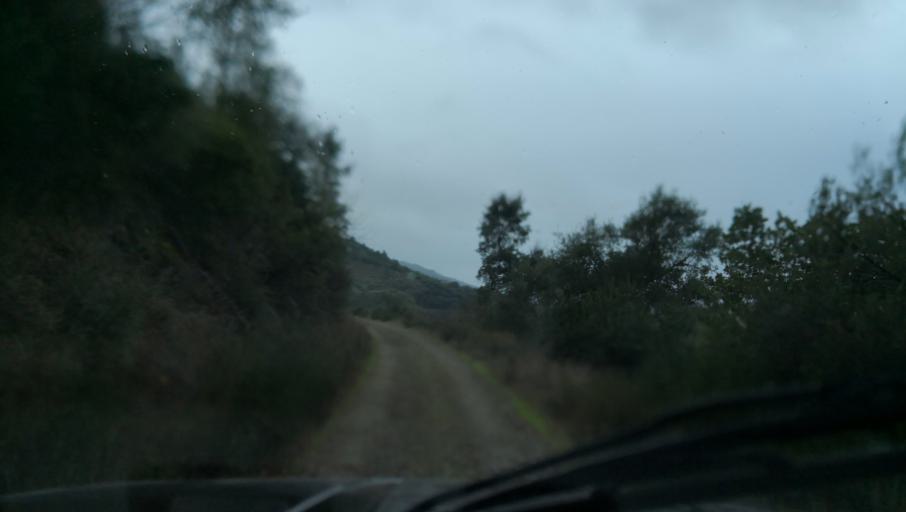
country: PT
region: Vila Real
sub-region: Vila Real
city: Vila Real
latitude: 41.2600
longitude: -7.7455
